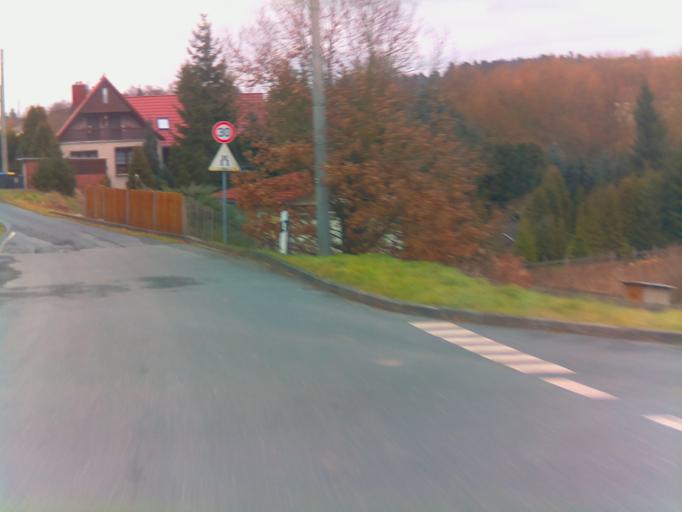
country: DE
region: Thuringia
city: Hummelshain
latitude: 50.7660
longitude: 11.6212
